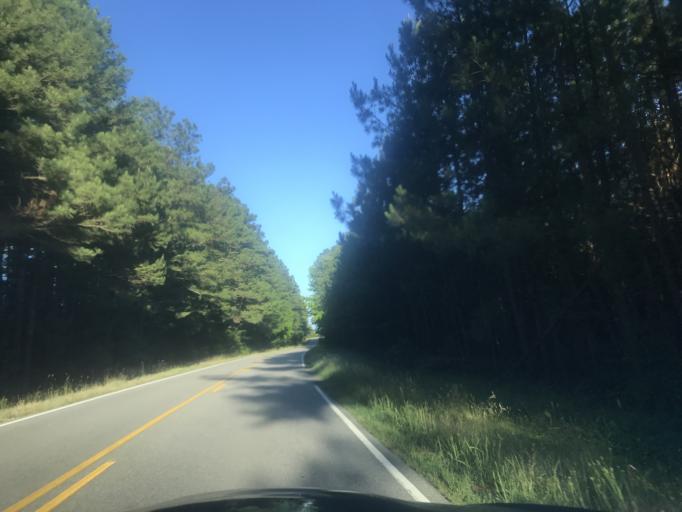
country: US
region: North Carolina
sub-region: Johnston County
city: Archer Lodge
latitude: 35.7309
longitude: -78.3965
